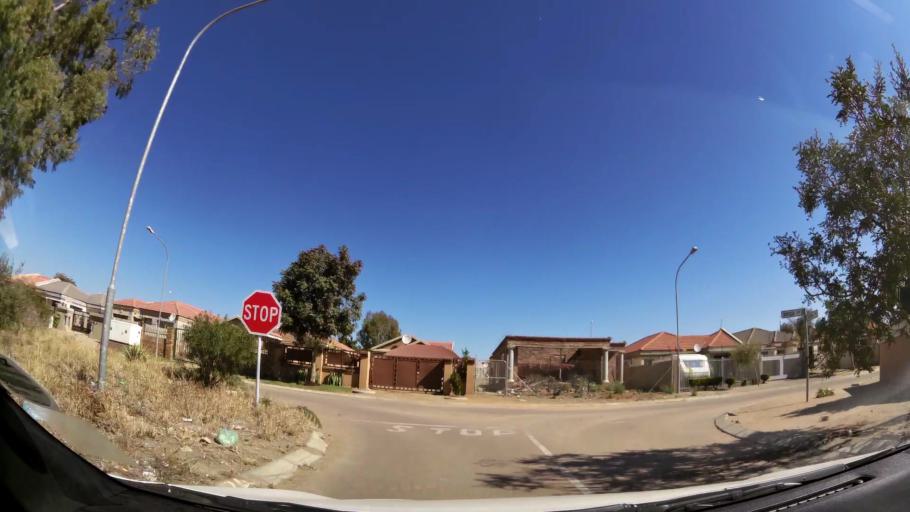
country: ZA
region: Limpopo
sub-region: Capricorn District Municipality
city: Polokwane
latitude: -23.8631
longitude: 29.4263
